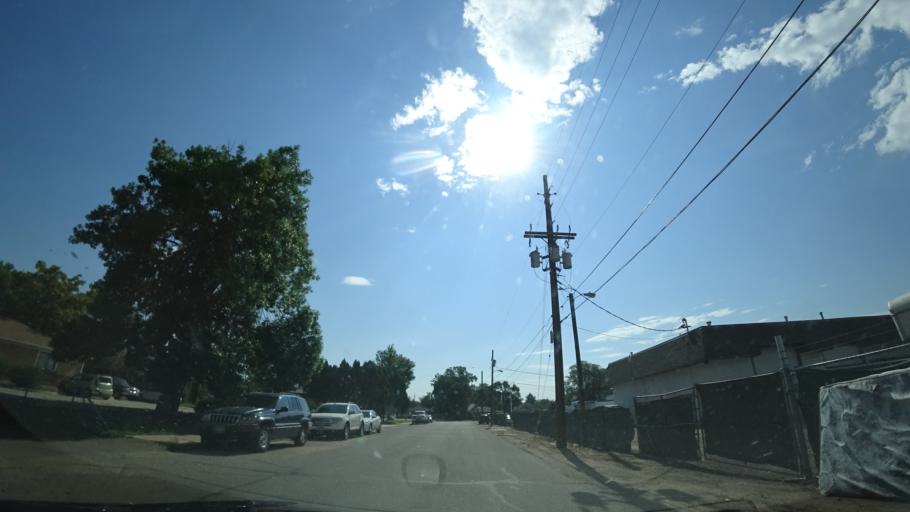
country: US
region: Colorado
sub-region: Jefferson County
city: Edgewater
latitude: 39.7231
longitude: -105.0546
